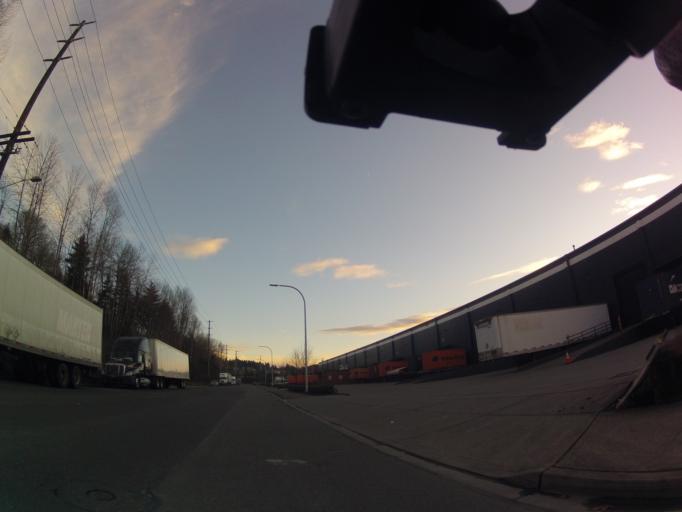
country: US
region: Washington
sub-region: King County
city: Renton
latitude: 47.4991
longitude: -122.1963
